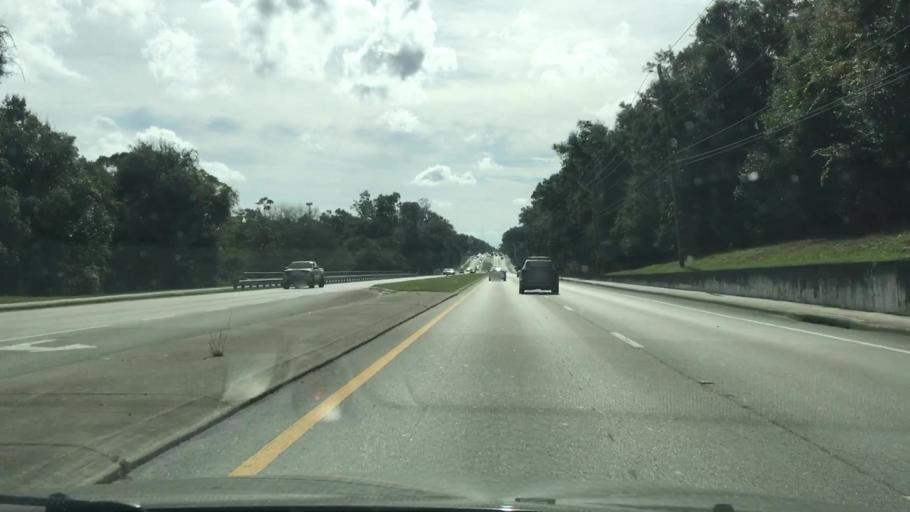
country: US
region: Florida
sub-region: Volusia County
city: North DeLand
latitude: 29.0497
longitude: -81.3250
